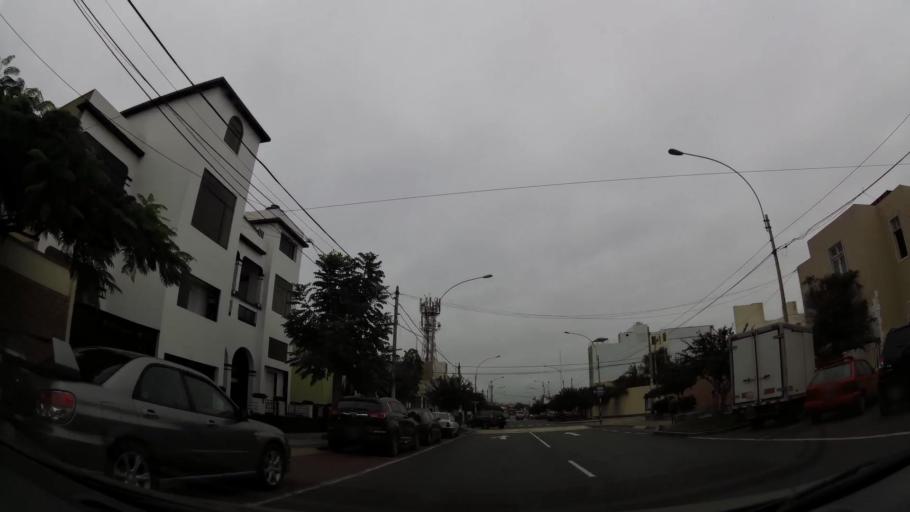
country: PE
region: Callao
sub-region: Callao
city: Callao
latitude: -12.0697
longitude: -77.1598
